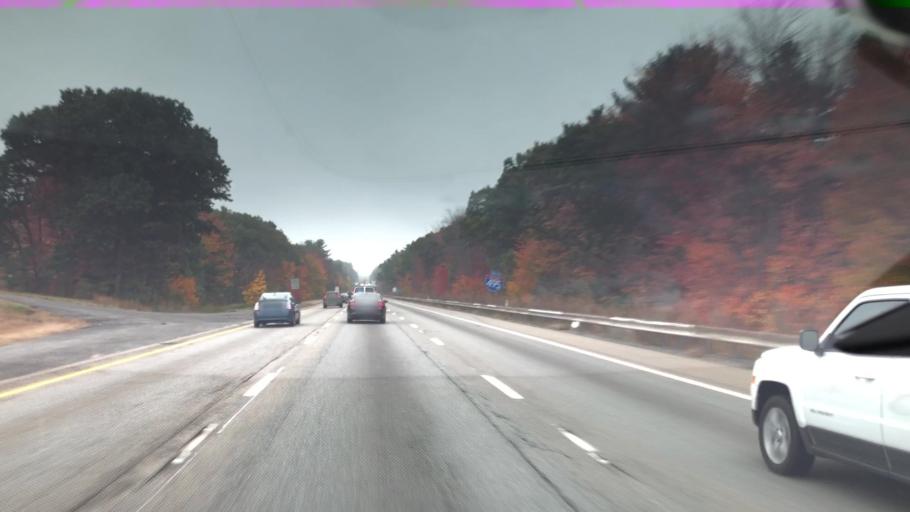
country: US
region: Massachusetts
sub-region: Middlesex County
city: Littleton Common
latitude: 42.5154
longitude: -71.5145
